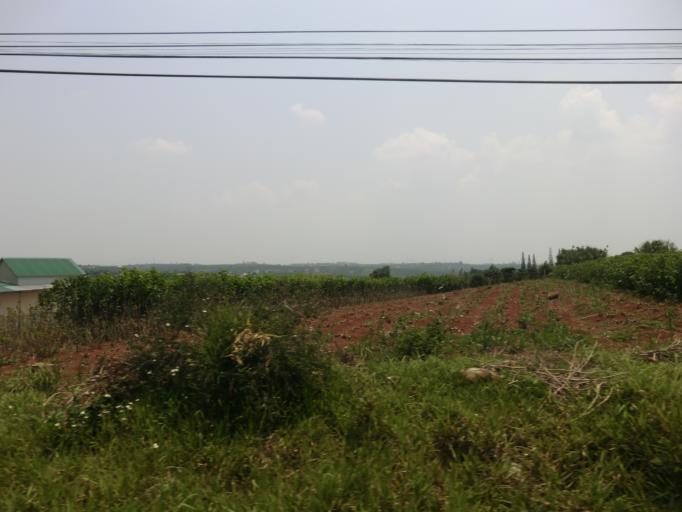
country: VN
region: Lam Dong
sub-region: Thanh Pho Bao Loc
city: Bao Loc
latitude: 11.5854
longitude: 107.7964
